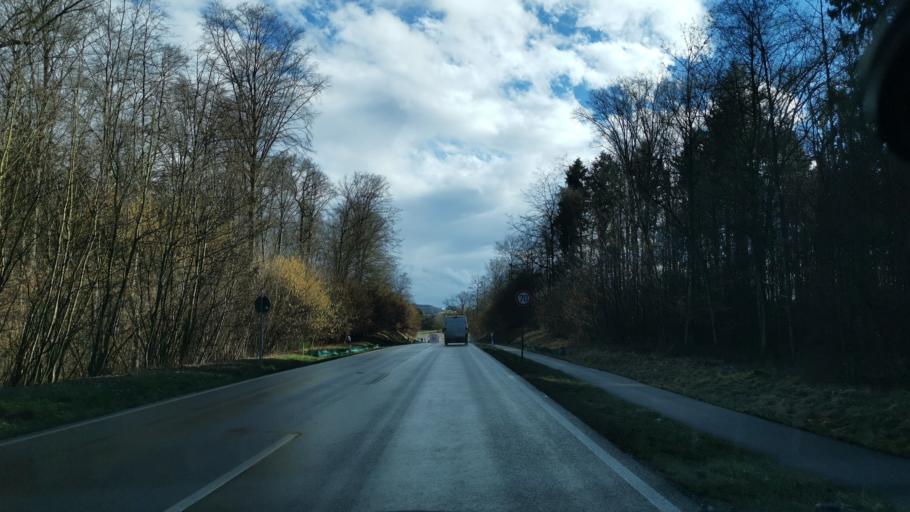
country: DE
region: Baden-Wuerttemberg
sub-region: Regierungsbezirk Stuttgart
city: Renningen
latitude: 48.7858
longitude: 8.9289
